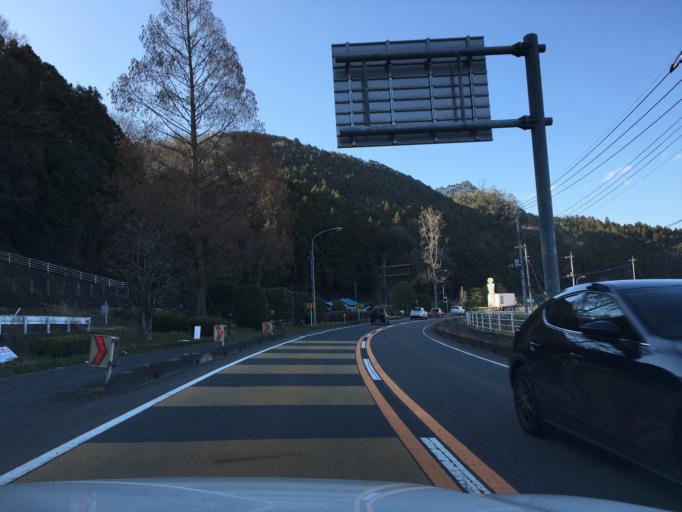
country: JP
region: Ibaraki
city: Omiya
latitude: 36.6353
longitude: 140.3915
